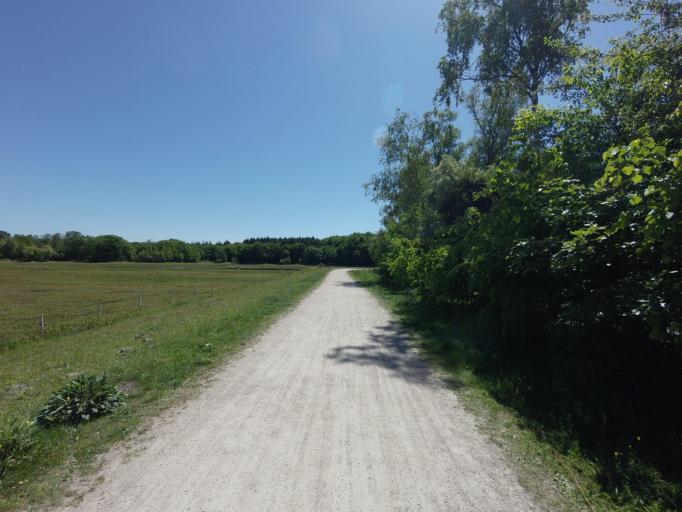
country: NL
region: North Holland
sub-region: Gemeente Hilversum
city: Hilversum
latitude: 52.2232
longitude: 5.2114
